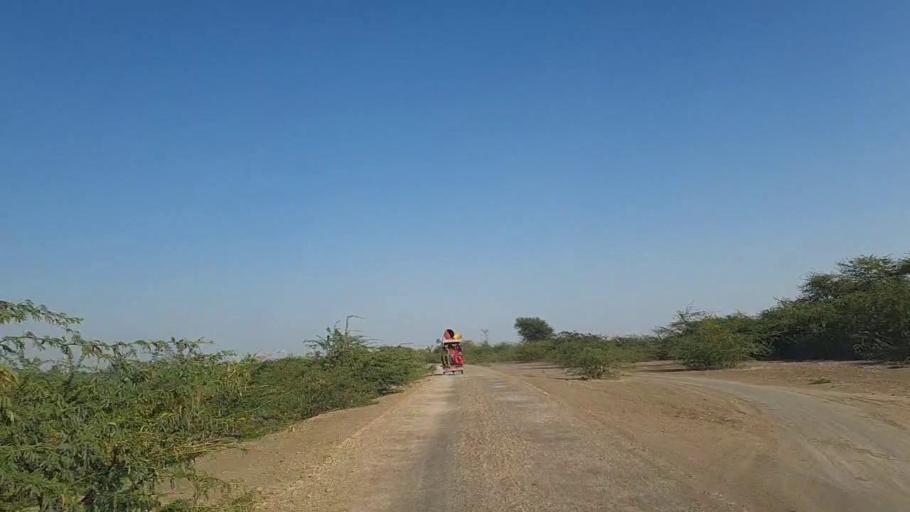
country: PK
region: Sindh
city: Naukot
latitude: 24.9458
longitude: 69.3392
